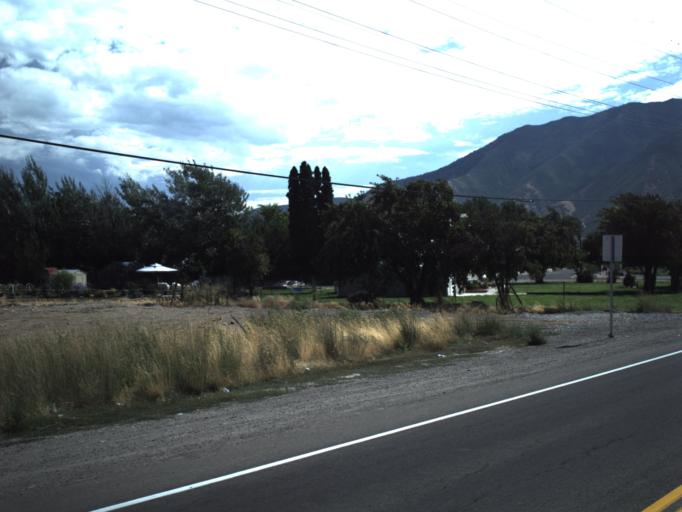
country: US
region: Utah
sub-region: Utah County
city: Spanish Fork
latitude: 40.1004
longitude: -111.6320
